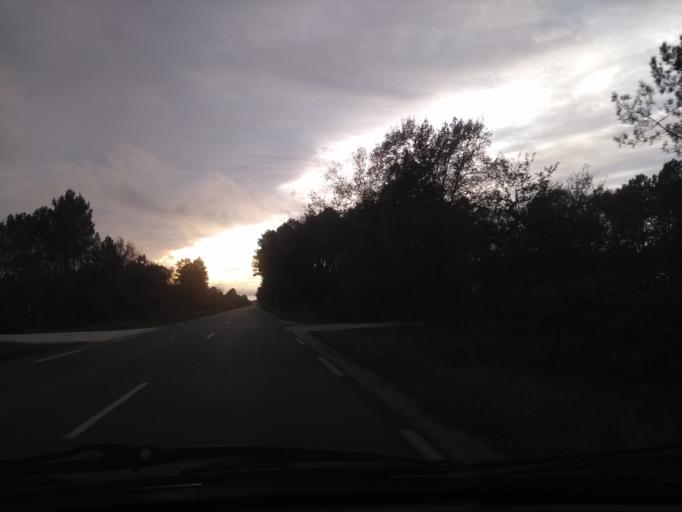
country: FR
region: Aquitaine
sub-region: Departement de la Gironde
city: Le Barp
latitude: 44.6061
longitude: -0.6962
